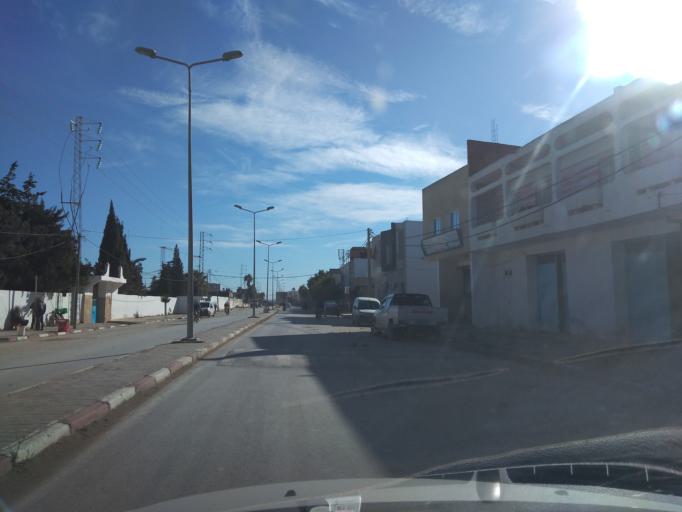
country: TN
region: Ariana
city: Qal'at al Andalus
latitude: 37.0582
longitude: 10.1199
